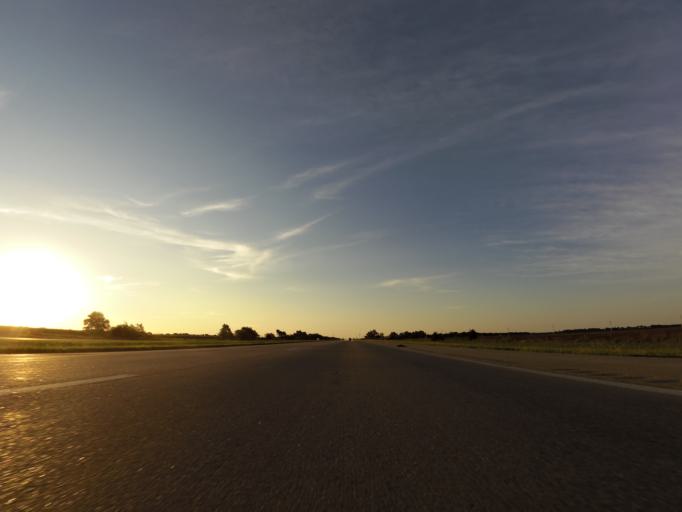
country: US
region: Kansas
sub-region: Reno County
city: South Hutchinson
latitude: 37.9600
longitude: -97.9128
